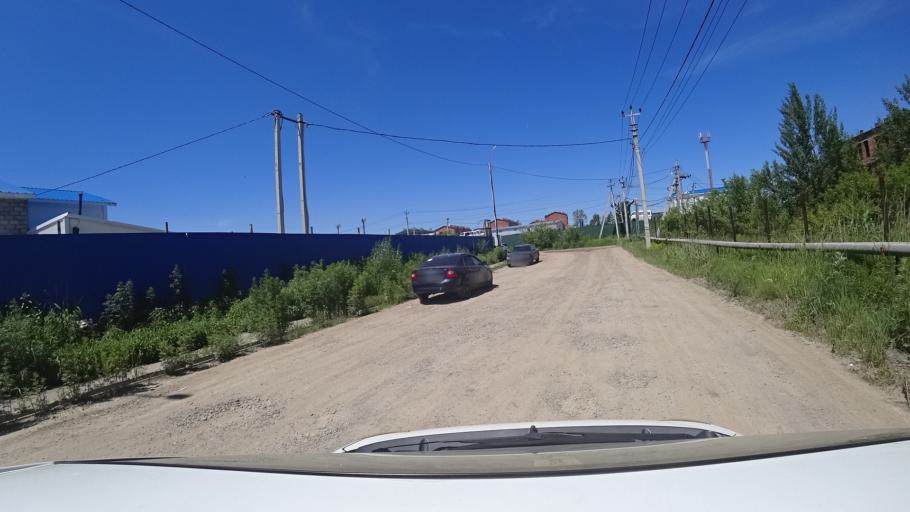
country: RU
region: Khabarovsk Krai
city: Topolevo
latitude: 48.5044
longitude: 135.1812
